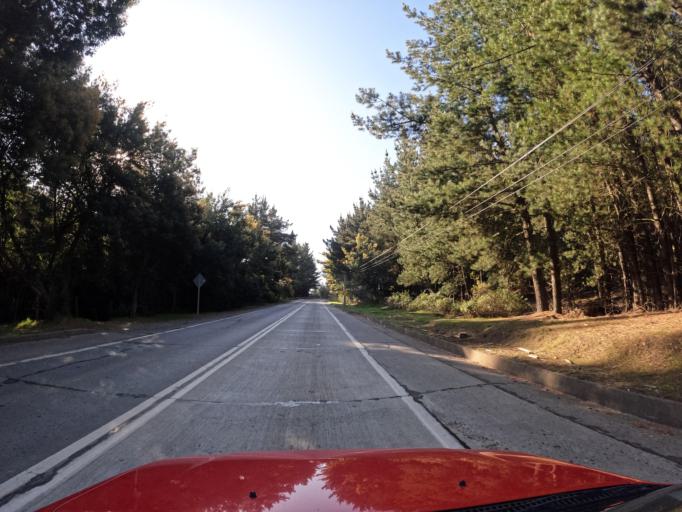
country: CL
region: Maule
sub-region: Provincia de Talca
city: Constitucion
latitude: -35.4348
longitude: -72.3345
